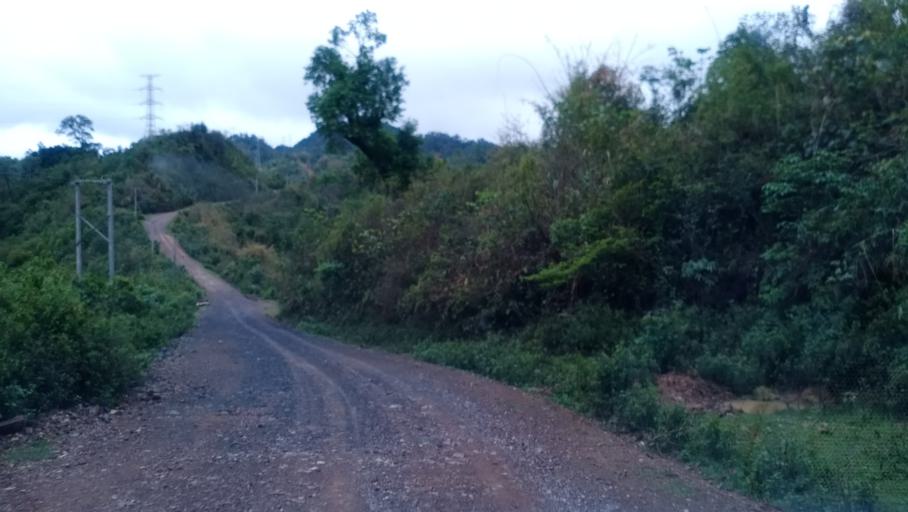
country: LA
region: Phongsali
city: Phongsali
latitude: 21.3399
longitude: 102.0840
